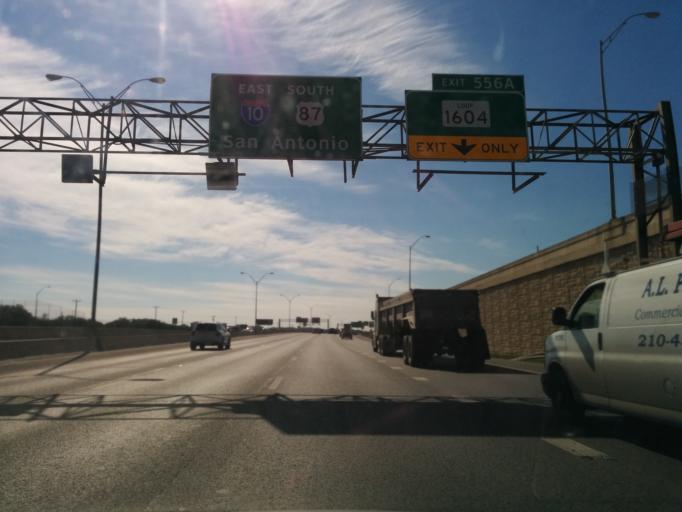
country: US
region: Texas
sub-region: Bexar County
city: Shavano Park
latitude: 29.6001
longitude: -98.6003
